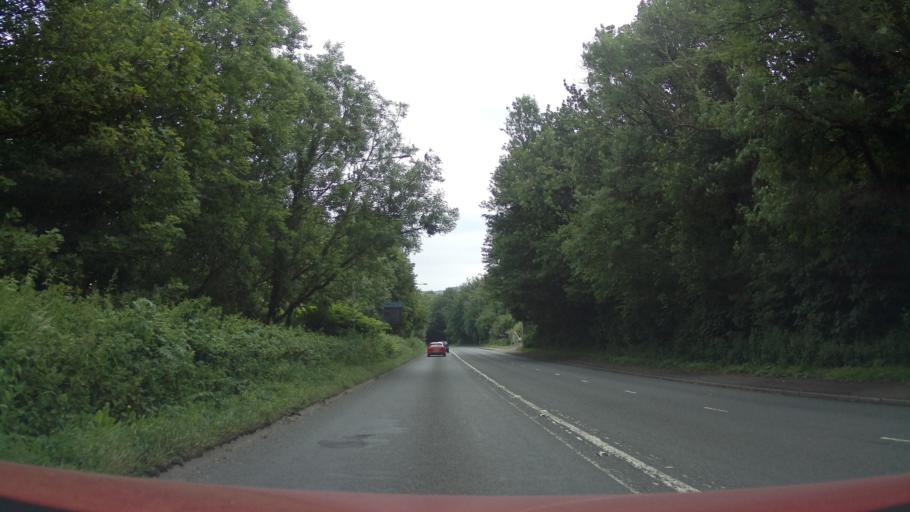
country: GB
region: Wales
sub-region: Cardiff
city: Radyr
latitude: 51.4654
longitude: -3.2827
